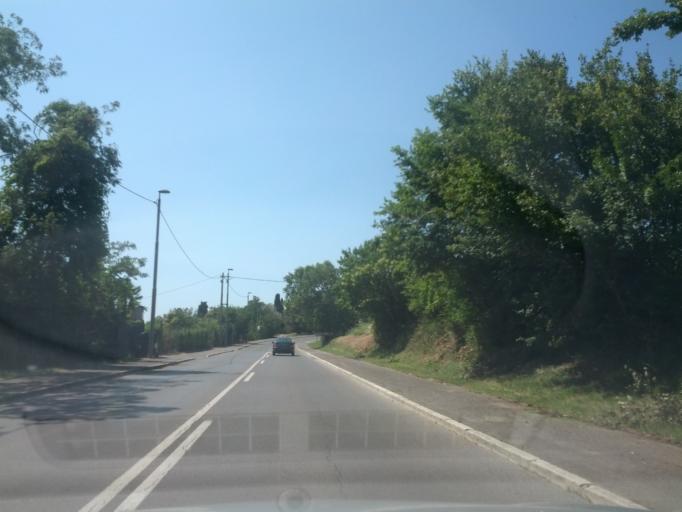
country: SI
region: Koper-Capodistria
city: Ankaran
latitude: 45.5757
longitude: 13.7405
